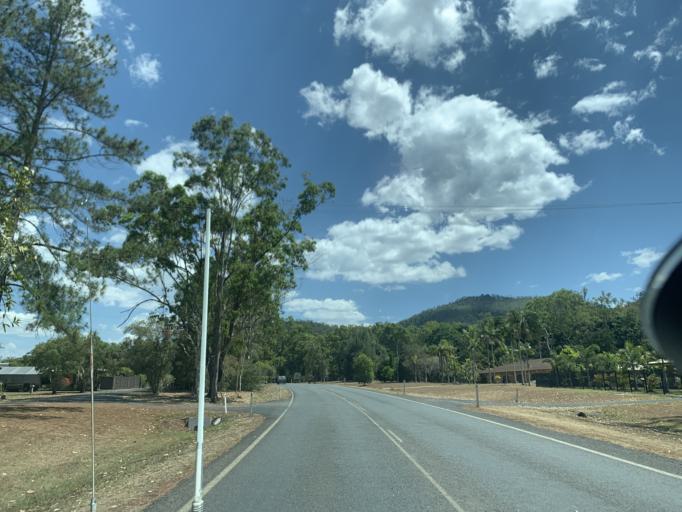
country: AU
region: Queensland
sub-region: Tablelands
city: Atherton
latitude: -17.2791
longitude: 145.4702
